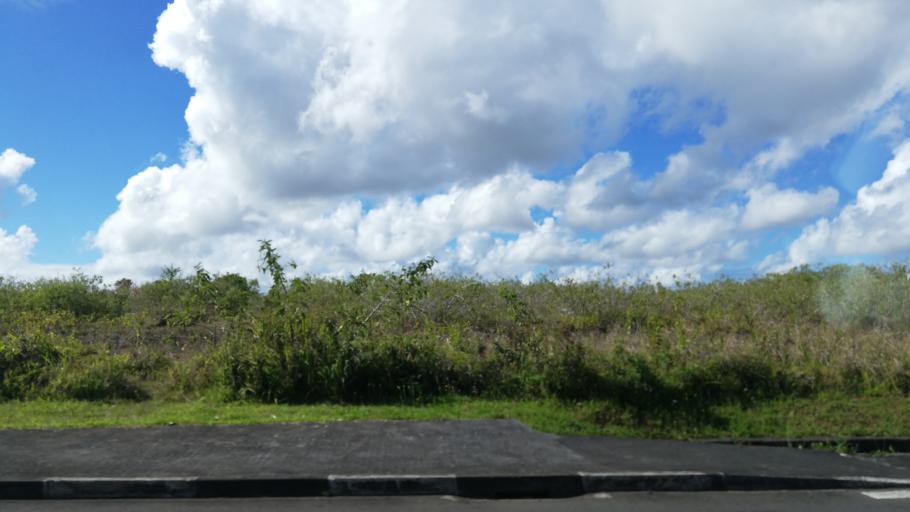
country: MU
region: Moka
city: Quartier Militaire
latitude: -20.2465
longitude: 57.5894
